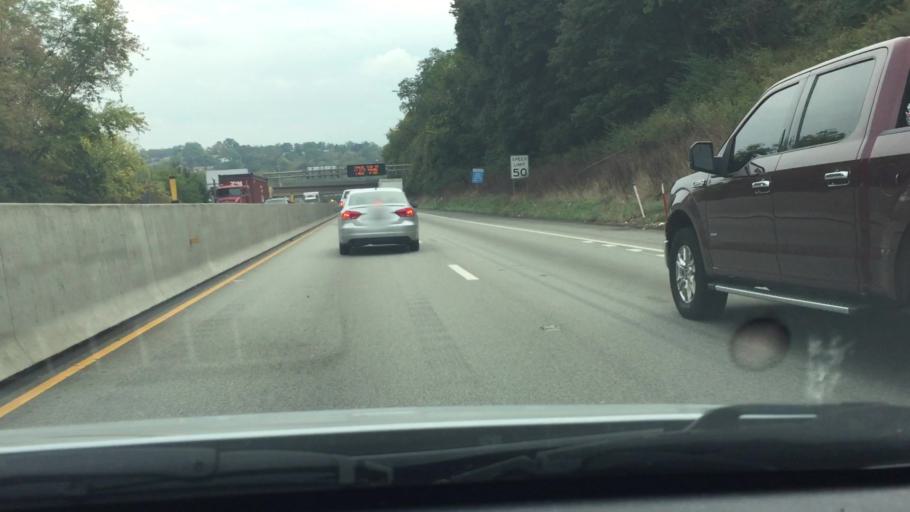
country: US
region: Pennsylvania
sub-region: Allegheny County
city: Green Tree
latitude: 40.4208
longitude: -80.0410
